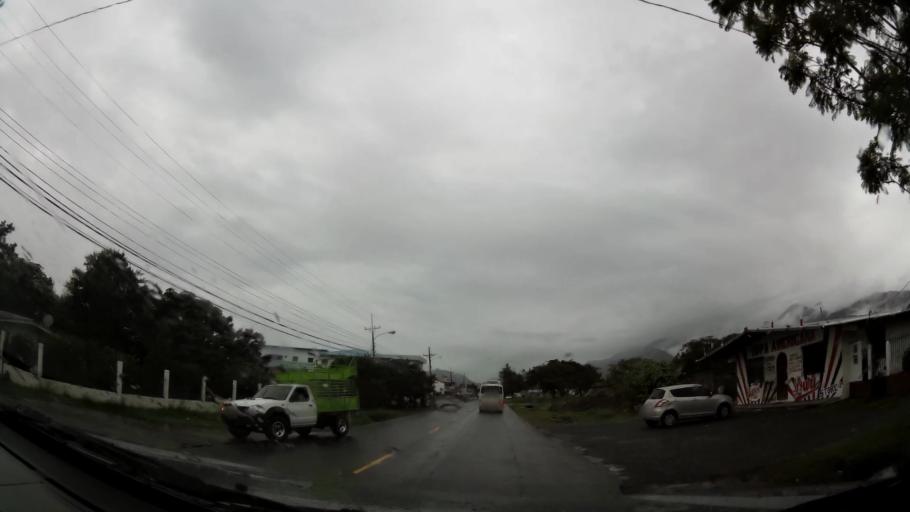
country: PA
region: Chiriqui
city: Volcan
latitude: 8.7814
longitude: -82.6457
